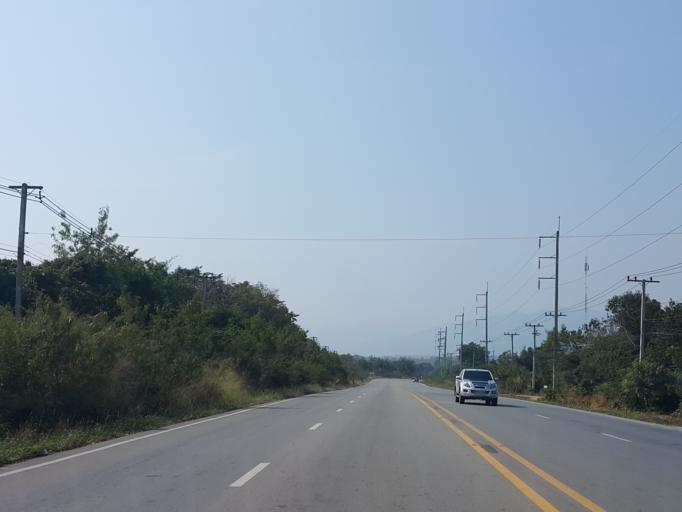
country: TH
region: Chiang Mai
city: Chom Thong
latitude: 18.3128
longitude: 98.6575
